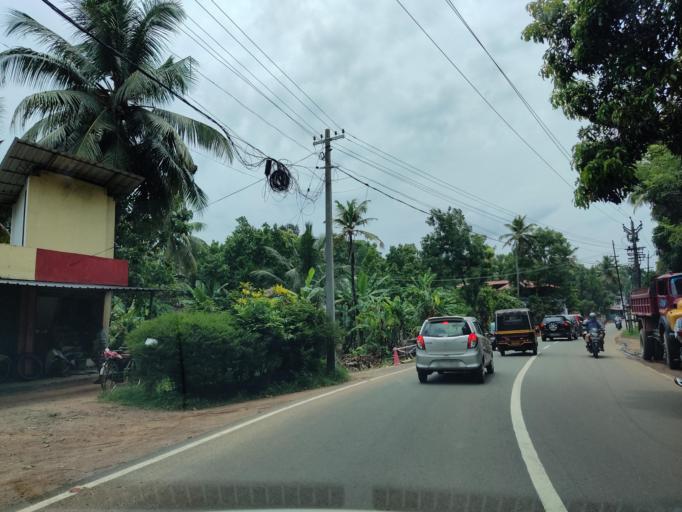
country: IN
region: Kerala
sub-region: Pattanamtitta
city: Adur
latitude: 9.2279
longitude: 76.6647
